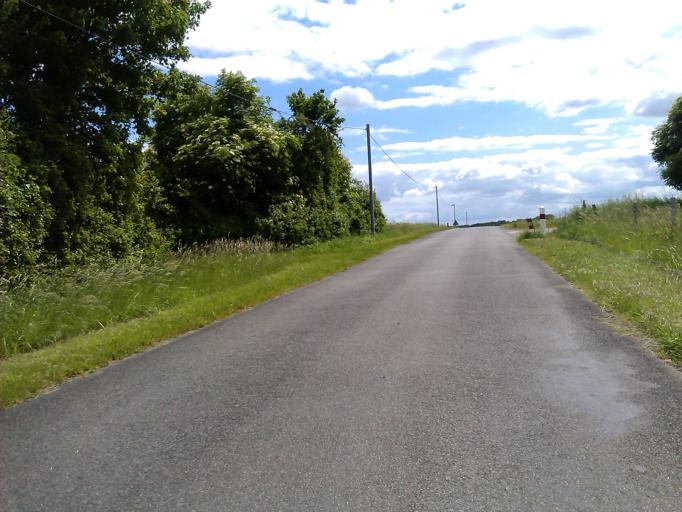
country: FR
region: Poitou-Charentes
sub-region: Departement de la Charente
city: Mansle
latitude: 45.9301
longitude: 0.2353
